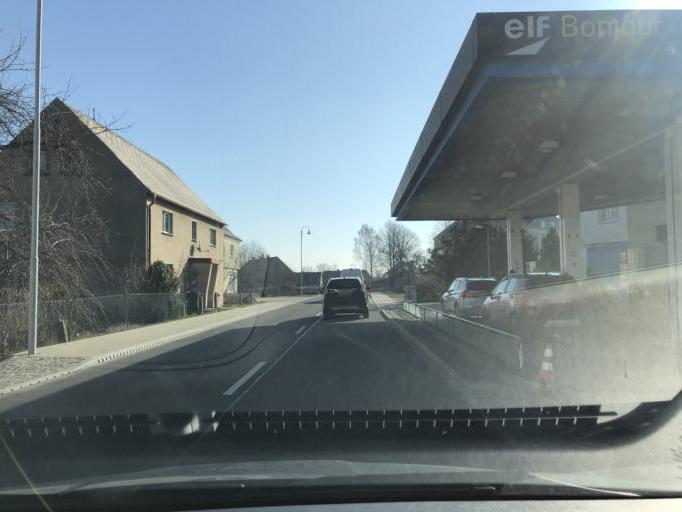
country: DE
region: Saxony
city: Rammenau
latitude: 51.1527
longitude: 14.1311
